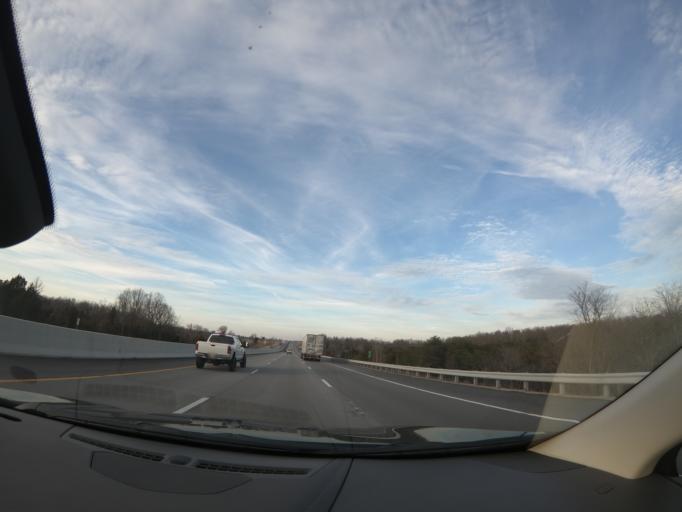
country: US
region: Kentucky
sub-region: Larue County
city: Hodgenville
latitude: 37.4745
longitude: -85.8815
